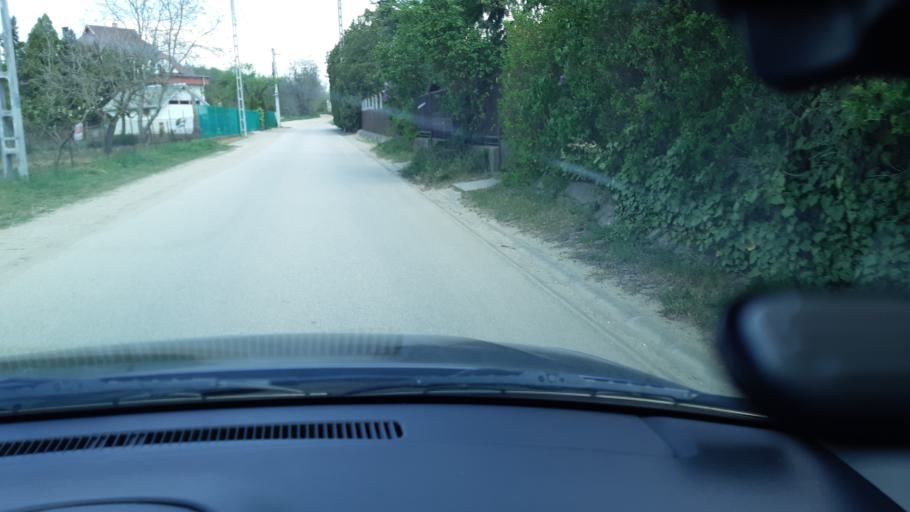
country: HU
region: Pest
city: Nagytarcsa
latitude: 47.5331
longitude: 19.2834
